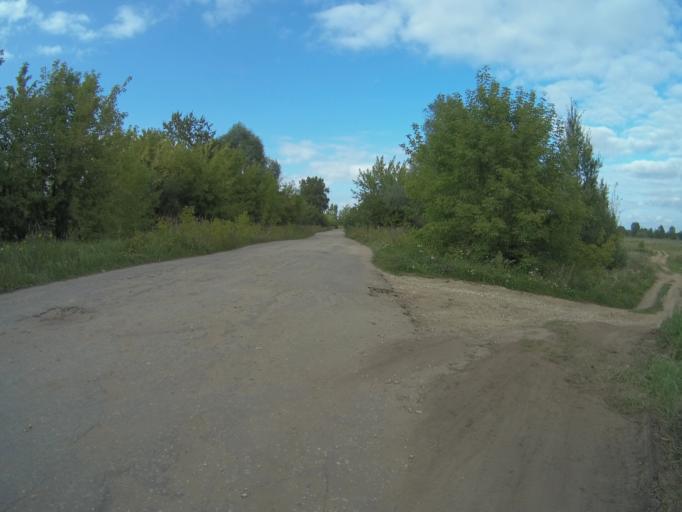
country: RU
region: Vladimir
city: Kommunar
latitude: 56.1239
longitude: 40.4220
